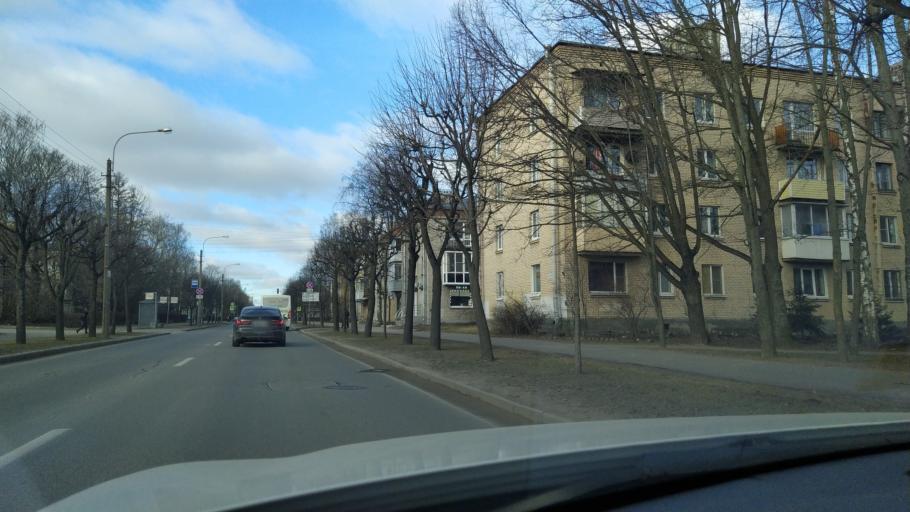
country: RU
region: St.-Petersburg
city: Pushkin
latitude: 59.7258
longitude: 30.4201
